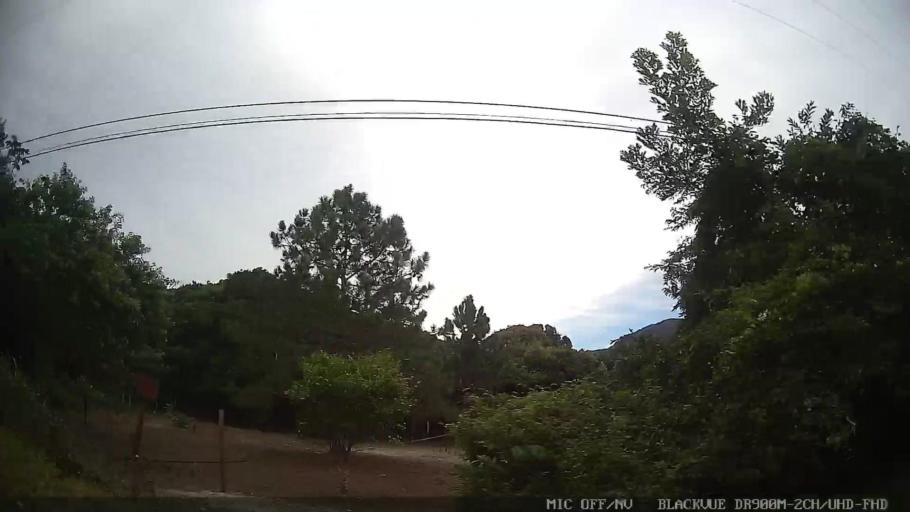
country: BR
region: Sao Paulo
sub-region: Iguape
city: Iguape
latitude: -24.6897
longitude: -47.5225
